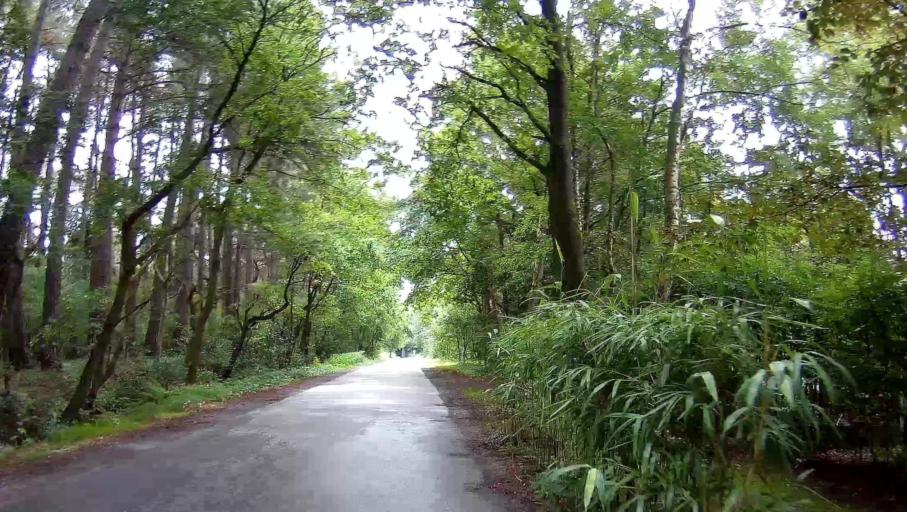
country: BE
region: Flanders
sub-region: Provincie Antwerpen
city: Balen
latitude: 51.2028
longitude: 5.2072
